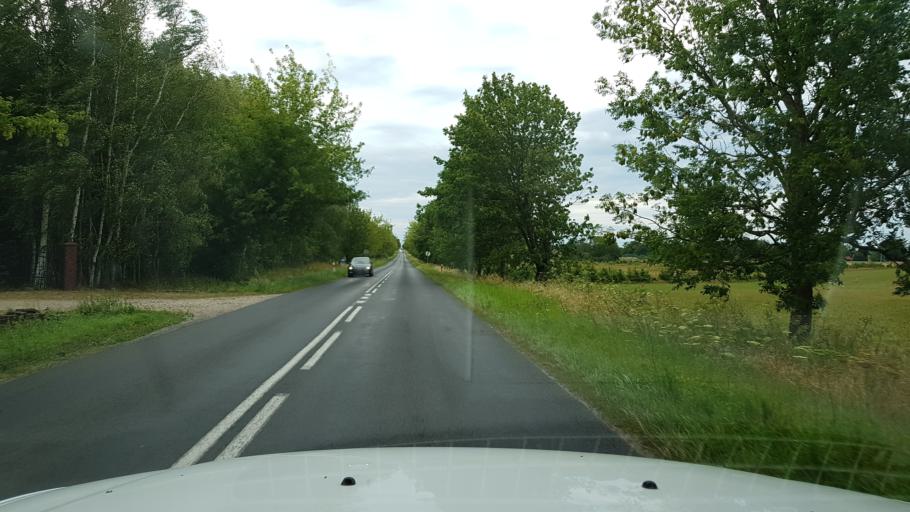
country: PL
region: West Pomeranian Voivodeship
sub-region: Powiat kolobrzeski
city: Kolobrzeg
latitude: 54.1468
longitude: 15.6441
